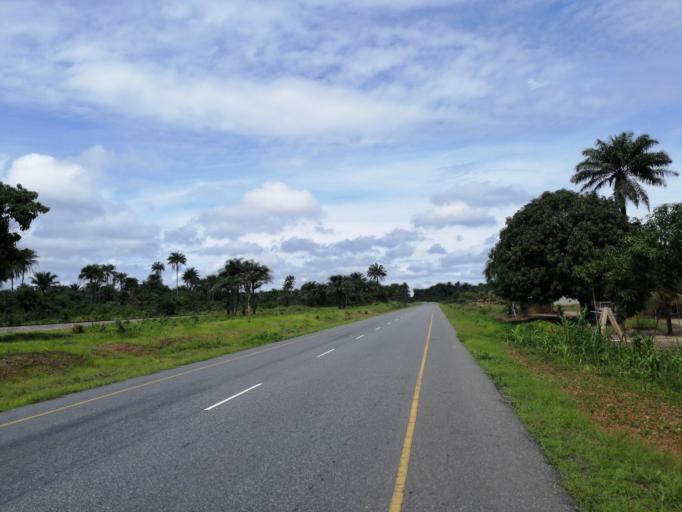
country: SL
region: Northern Province
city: Pepel
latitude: 8.7234
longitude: -12.9564
